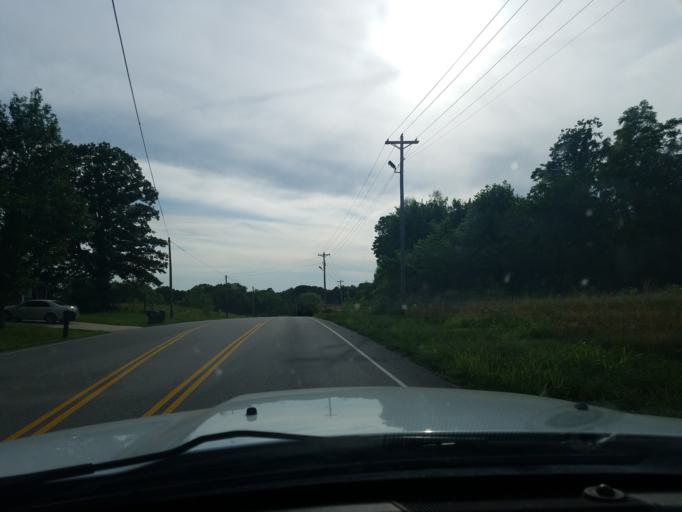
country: US
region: Tennessee
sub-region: Putnam County
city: Cookeville
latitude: 36.1295
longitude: -85.5464
